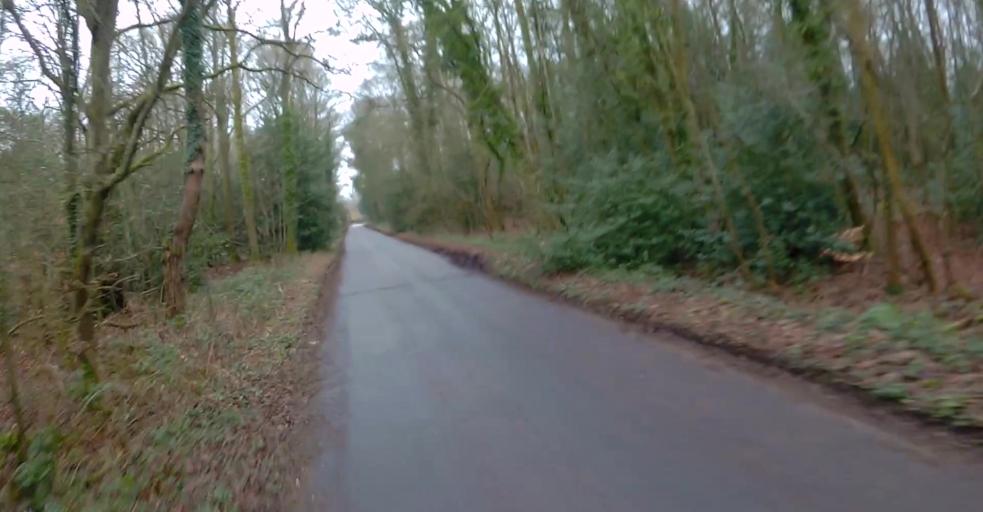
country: GB
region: England
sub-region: Hampshire
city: Hook
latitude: 51.3158
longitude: -0.9482
